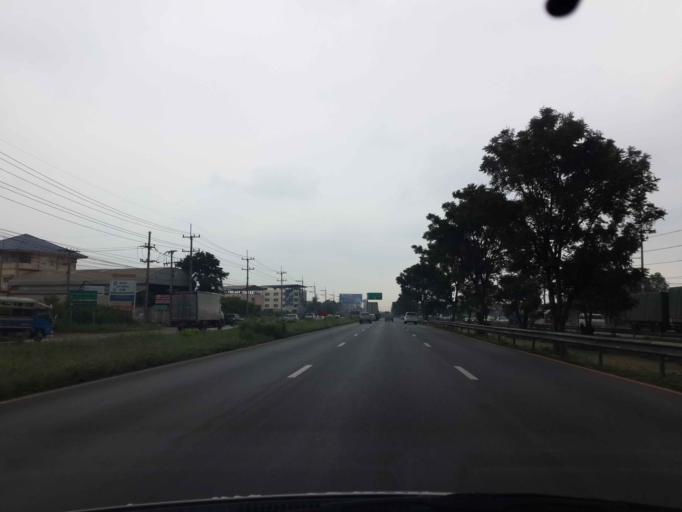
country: TH
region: Samut Sakhon
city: Samut Sakhon
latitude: 13.5746
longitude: 100.2971
